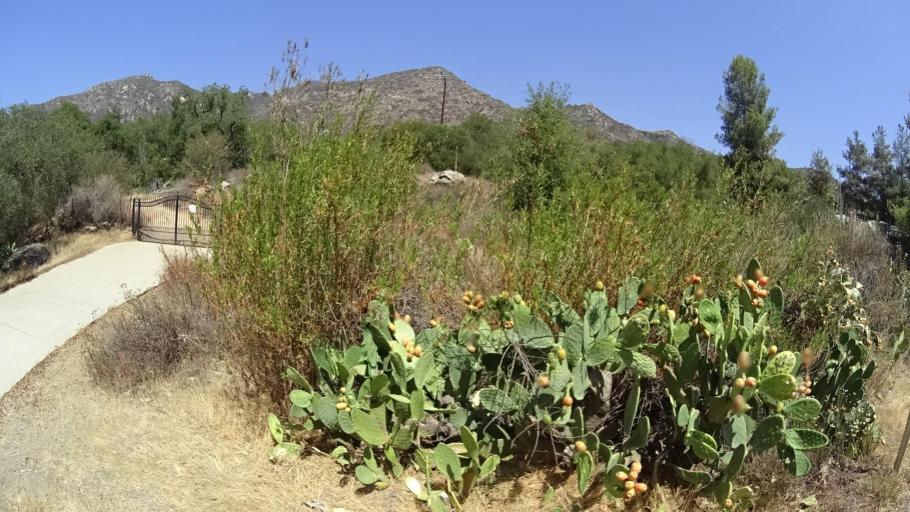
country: US
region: California
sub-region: San Diego County
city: Fallbrook
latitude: 33.4609
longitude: -117.2877
